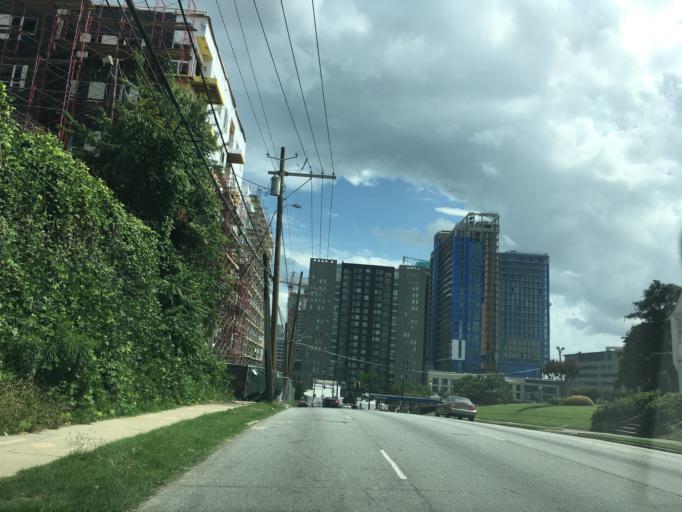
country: US
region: Georgia
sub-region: Fulton County
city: Atlanta
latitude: 33.7827
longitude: -84.3891
